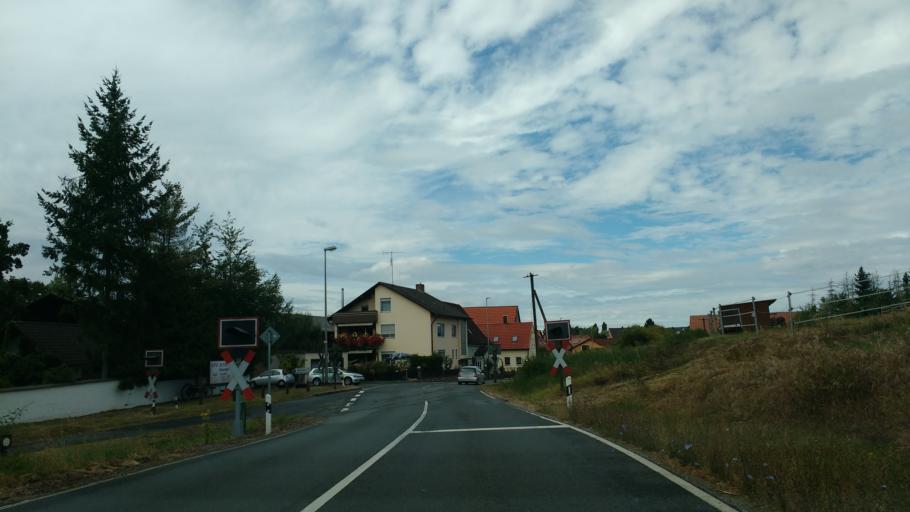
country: DE
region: Bavaria
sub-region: Upper Franconia
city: Schlusselfeld
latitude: 49.7491
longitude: 10.6310
